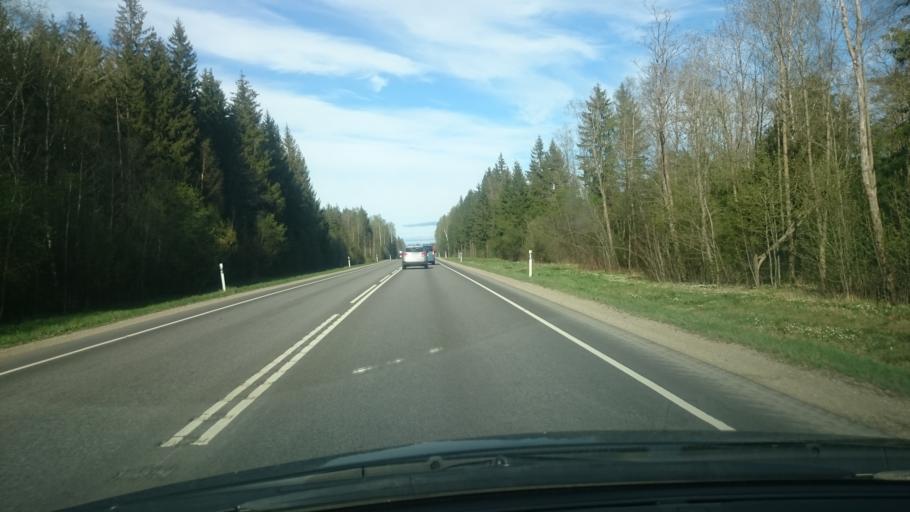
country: EE
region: Ida-Virumaa
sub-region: Toila vald
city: Toila
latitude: 59.3776
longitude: 27.5382
